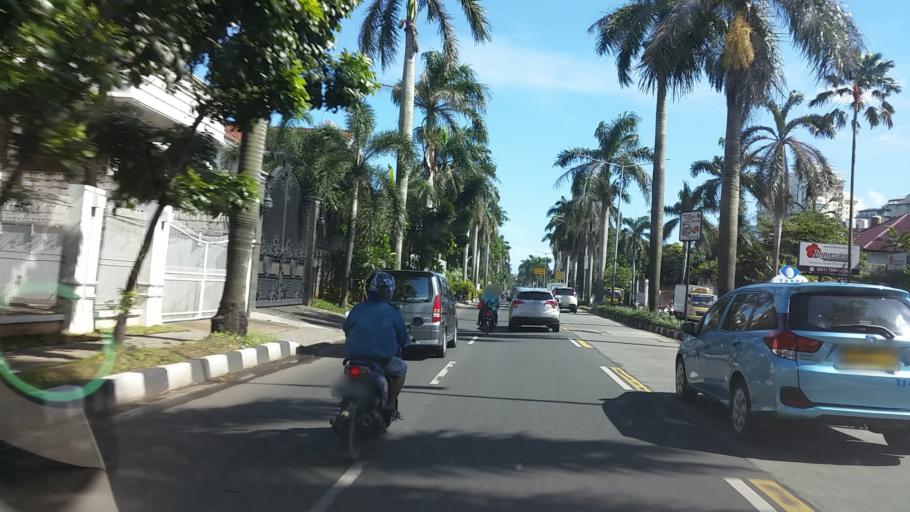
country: ID
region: Banten
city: South Tangerang
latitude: -6.2767
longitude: 106.7817
